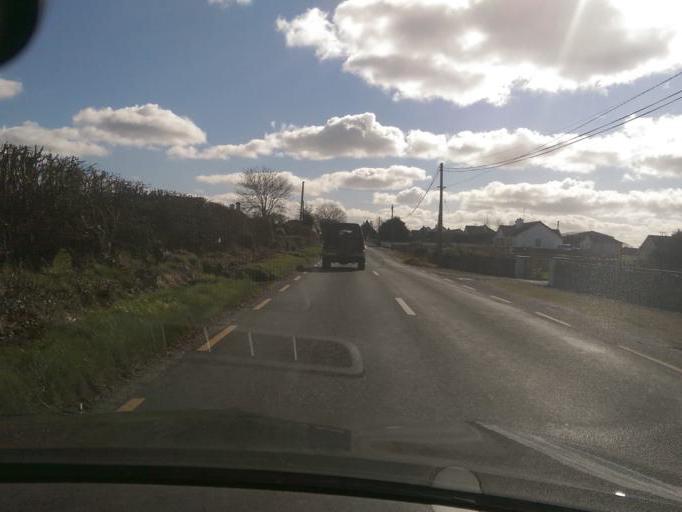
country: IE
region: Connaught
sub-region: County Galway
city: Athenry
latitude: 53.3220
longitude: -8.7633
